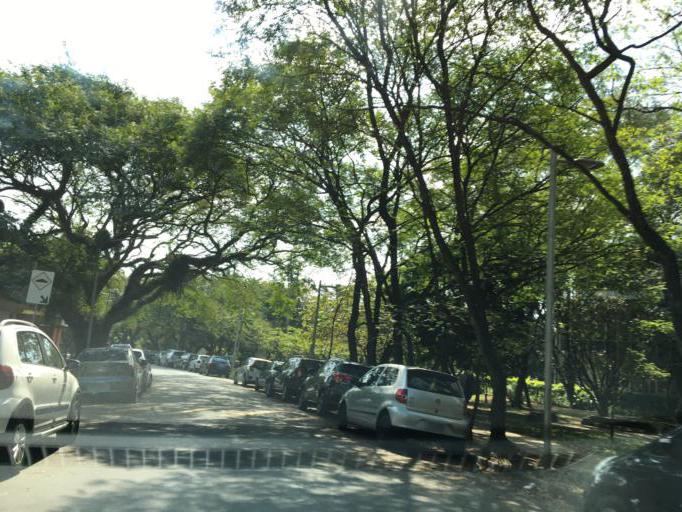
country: BR
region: Sao Paulo
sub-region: Osasco
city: Osasco
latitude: -23.5623
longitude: -46.7280
